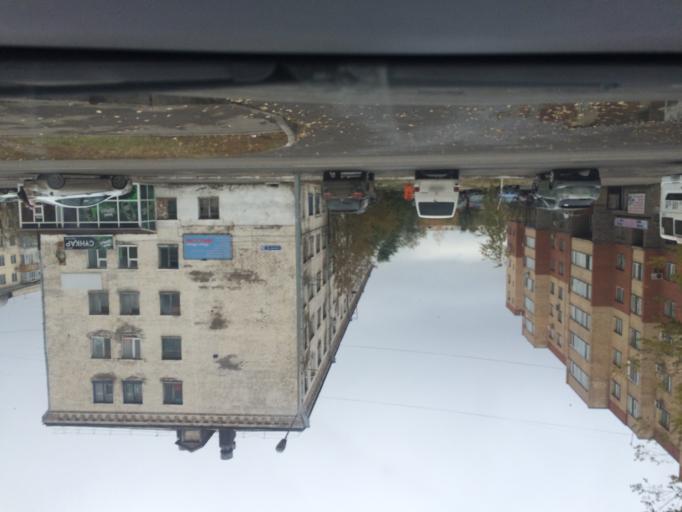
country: KZ
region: Astana Qalasy
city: Astana
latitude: 51.1893
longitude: 71.4188
